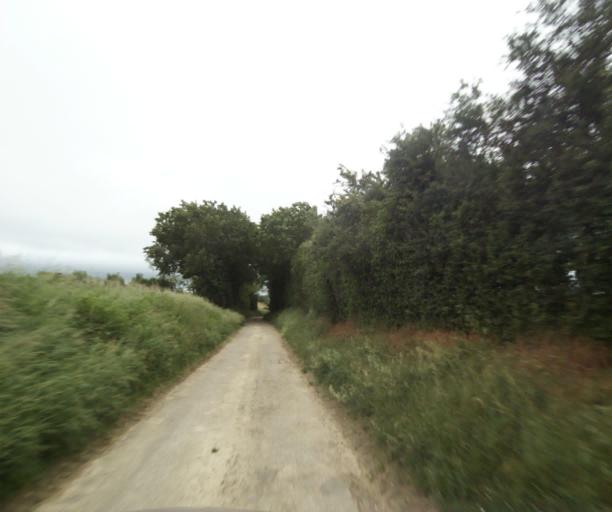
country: FR
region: Rhone-Alpes
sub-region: Departement de l'Ain
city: Miribel
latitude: 45.8461
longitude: 4.9445
